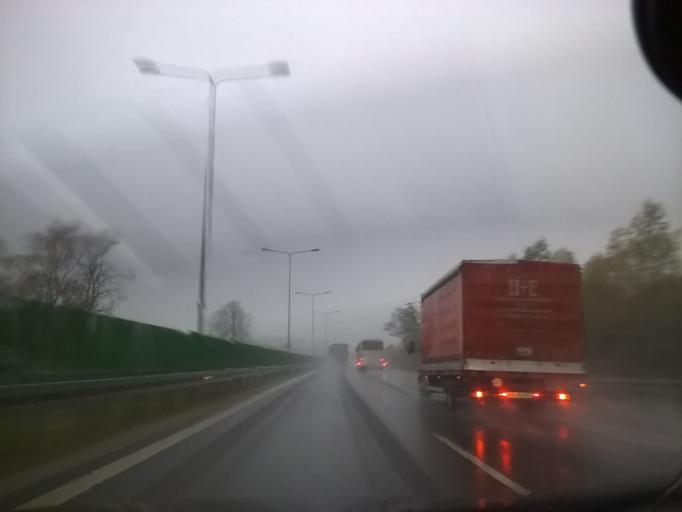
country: PL
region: Warmian-Masurian Voivodeship
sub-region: Powiat elblaski
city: Gronowo Gorne
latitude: 54.1357
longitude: 19.4335
